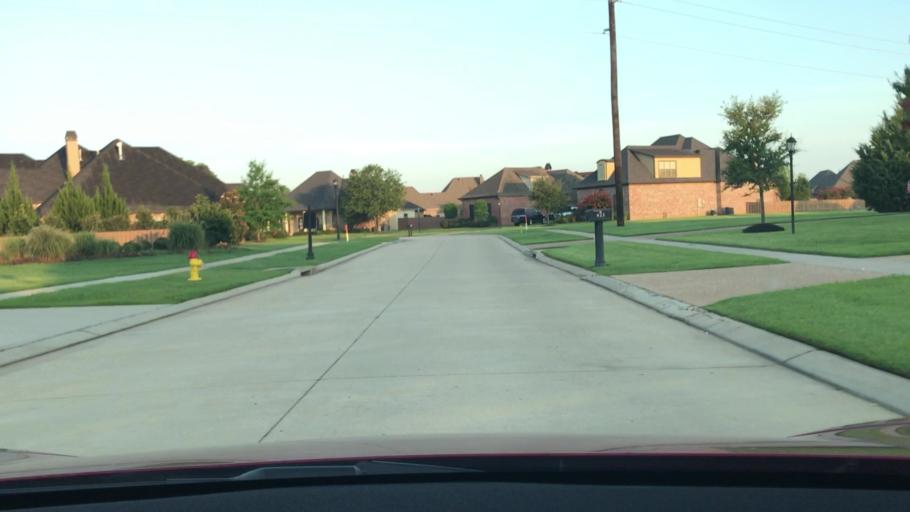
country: US
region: Louisiana
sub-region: Bossier Parish
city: Bossier City
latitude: 32.3936
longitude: -93.7028
